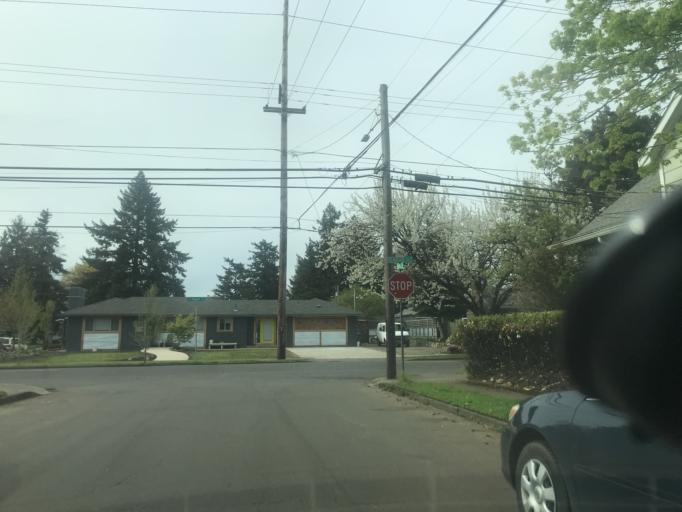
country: US
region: Oregon
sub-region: Multnomah County
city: Lents
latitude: 45.4905
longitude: -122.5848
